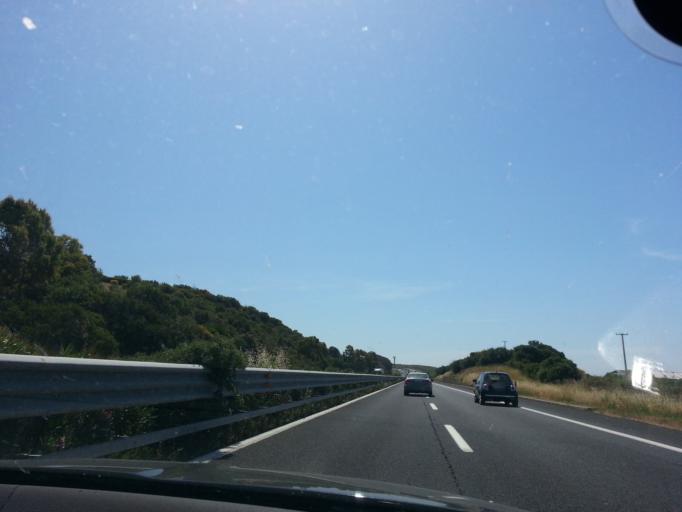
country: IT
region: Latium
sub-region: Citta metropolitana di Roma Capitale
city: Santa Marinella
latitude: 42.0440
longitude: 11.8414
